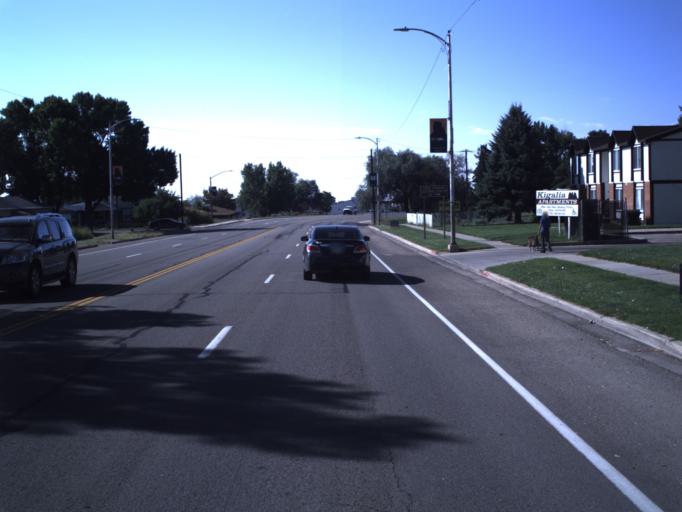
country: US
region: Utah
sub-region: San Juan County
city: Blanding
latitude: 37.6193
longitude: -109.4781
